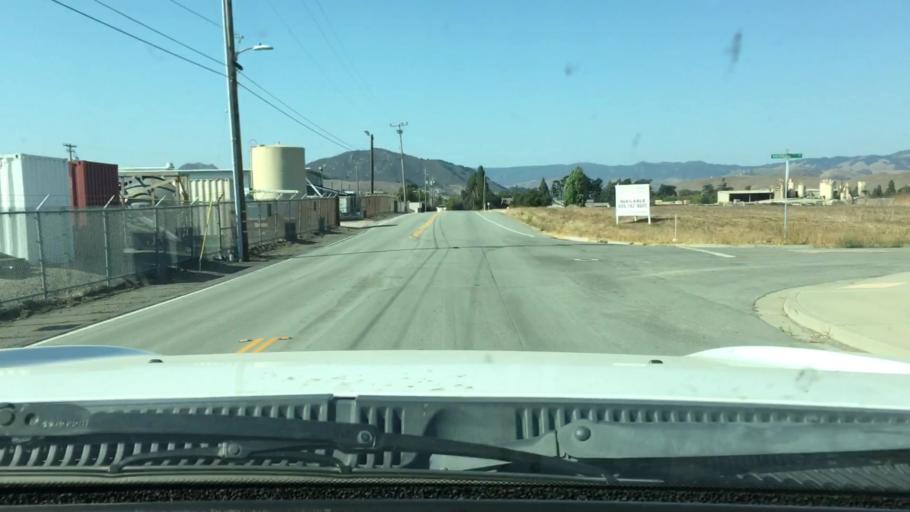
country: US
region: California
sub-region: San Luis Obispo County
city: San Luis Obispo
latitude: 35.2363
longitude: -120.6736
